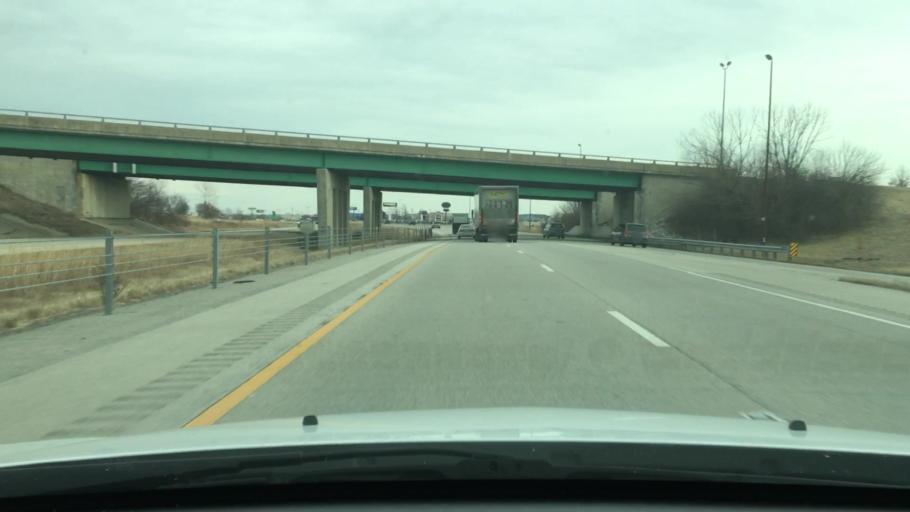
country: US
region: Illinois
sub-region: Sangamon County
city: Jerome
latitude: 39.7427
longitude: -89.7069
